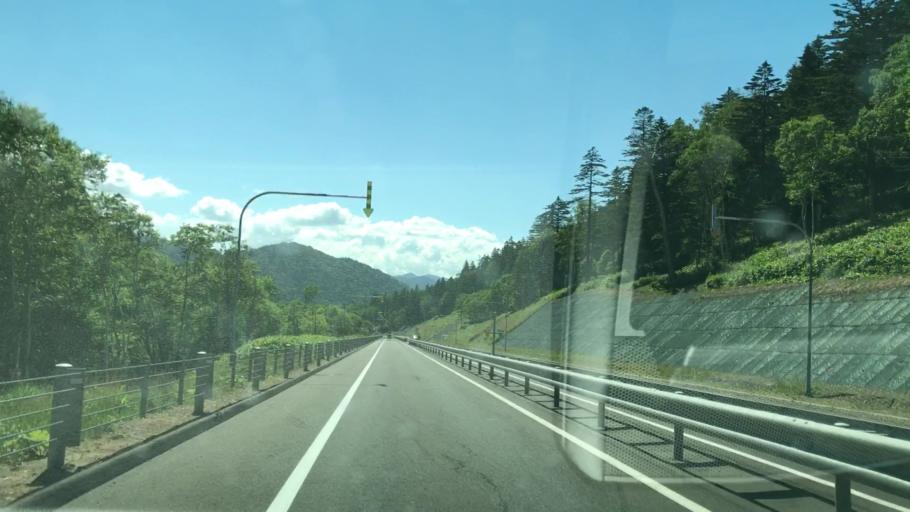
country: JP
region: Hokkaido
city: Otofuke
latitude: 42.9811
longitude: 142.7352
